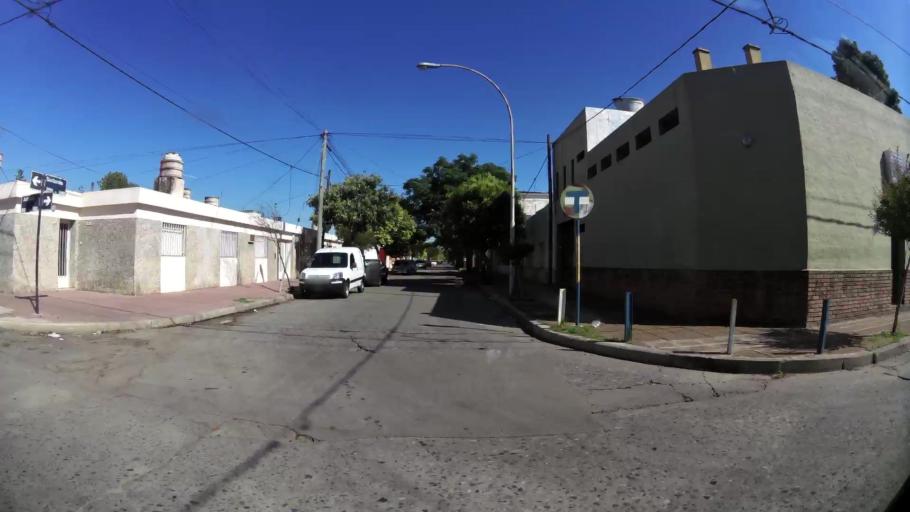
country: AR
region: Cordoba
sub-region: Departamento de Capital
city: Cordoba
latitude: -31.4392
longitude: -64.1589
